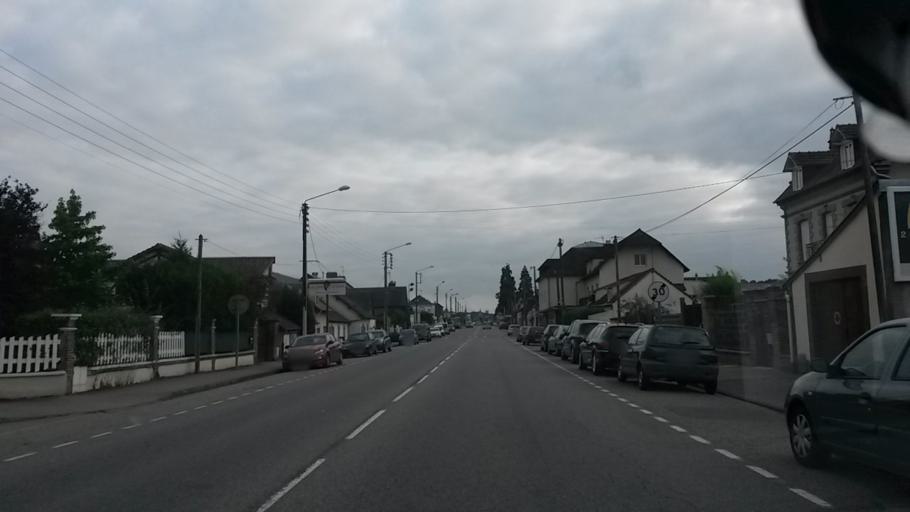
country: FR
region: Haute-Normandie
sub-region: Departement de l'Eure
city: Gravigny
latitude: 49.0436
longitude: 1.1602
